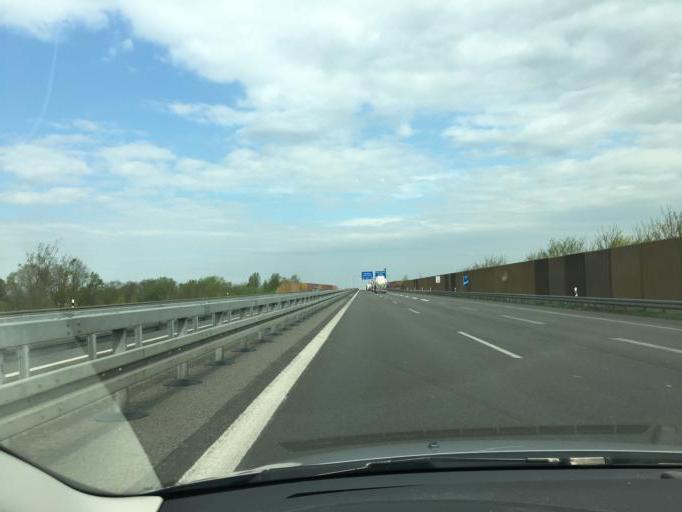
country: DE
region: Saxony-Anhalt
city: Peissen
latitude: 51.4980
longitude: 12.0537
